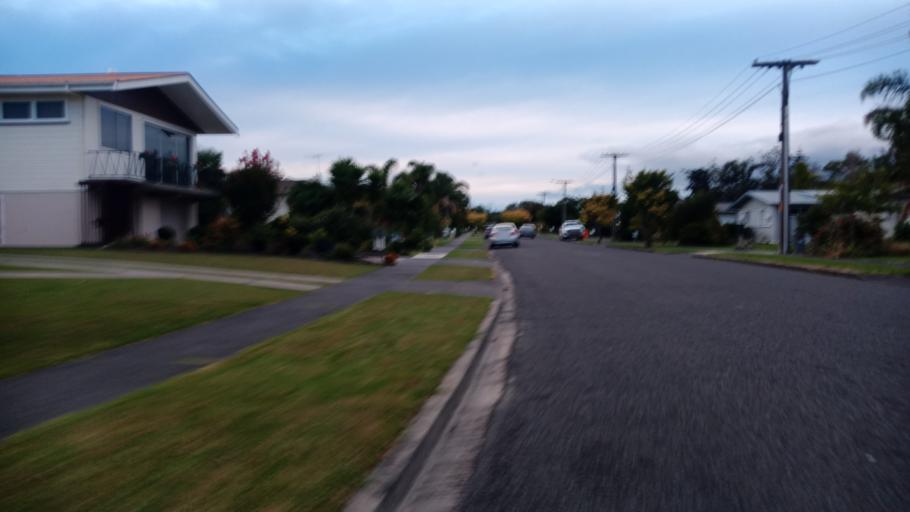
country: NZ
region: Gisborne
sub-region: Gisborne District
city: Gisborne
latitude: -38.6491
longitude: 178.0076
